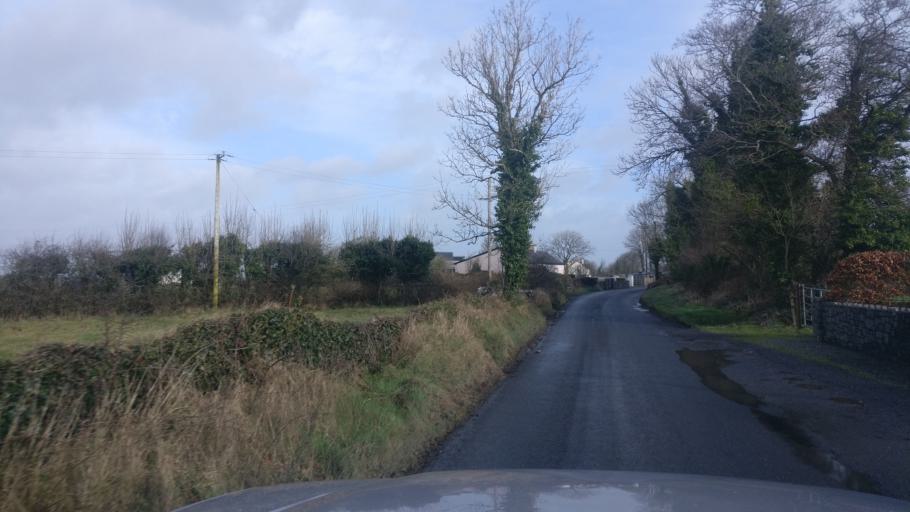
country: IE
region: Connaught
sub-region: County Galway
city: Loughrea
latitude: 53.2752
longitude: -8.5860
